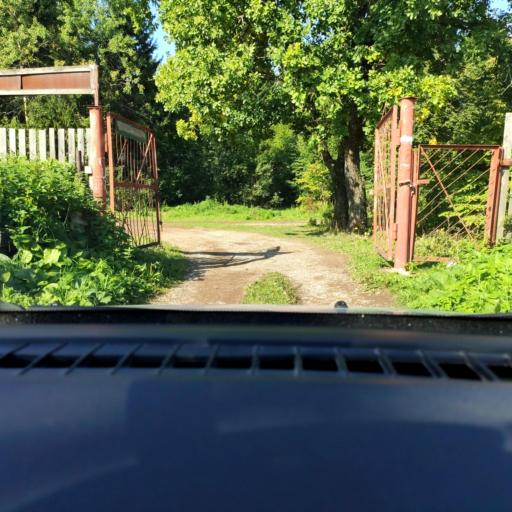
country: RU
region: Perm
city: Novyye Lyady
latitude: 58.0615
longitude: 56.5787
